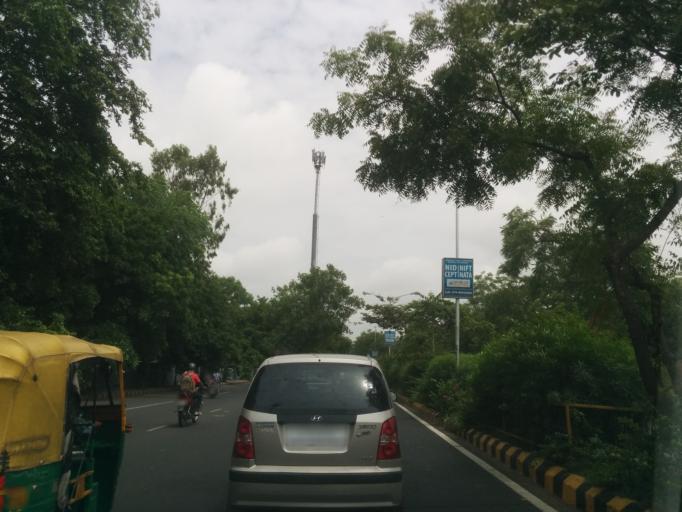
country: IN
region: Gujarat
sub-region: Ahmadabad
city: Ahmedabad
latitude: 23.0366
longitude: 72.5486
